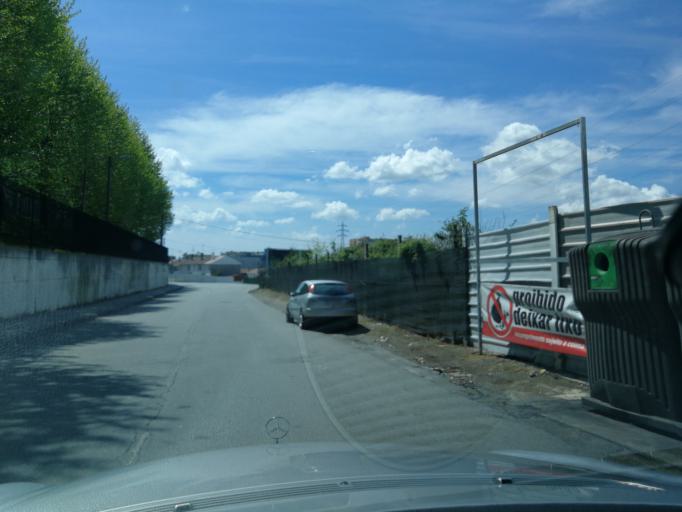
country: PT
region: Braga
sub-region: Vila Nova de Famalicao
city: Vila Nova de Famalicao
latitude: 41.4175
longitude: -8.5147
